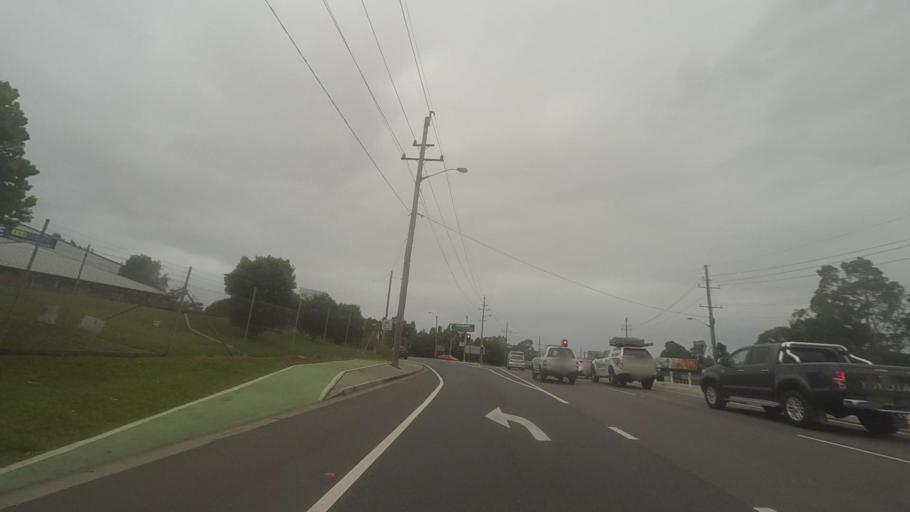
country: AU
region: New South Wales
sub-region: Newcastle
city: Mayfield West
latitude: -32.8815
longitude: 151.7187
